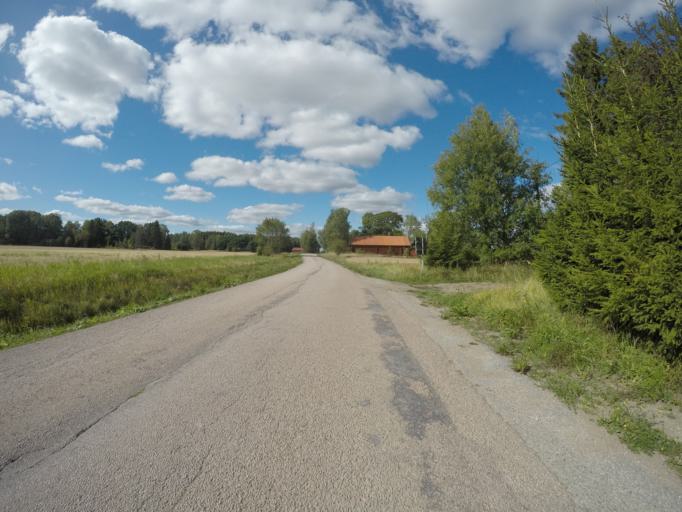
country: SE
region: Vaestmanland
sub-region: Hallstahammars Kommun
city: Kolback
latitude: 59.5111
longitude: 16.1890
